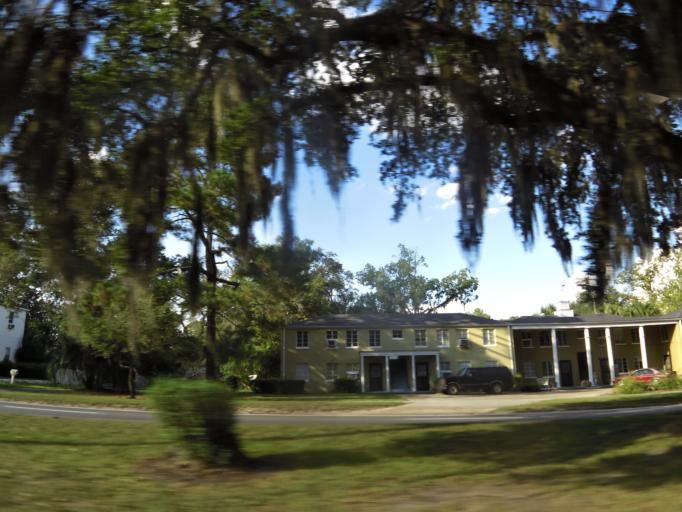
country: US
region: Georgia
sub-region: Brooks County
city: Quitman
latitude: 30.7850
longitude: -83.5627
